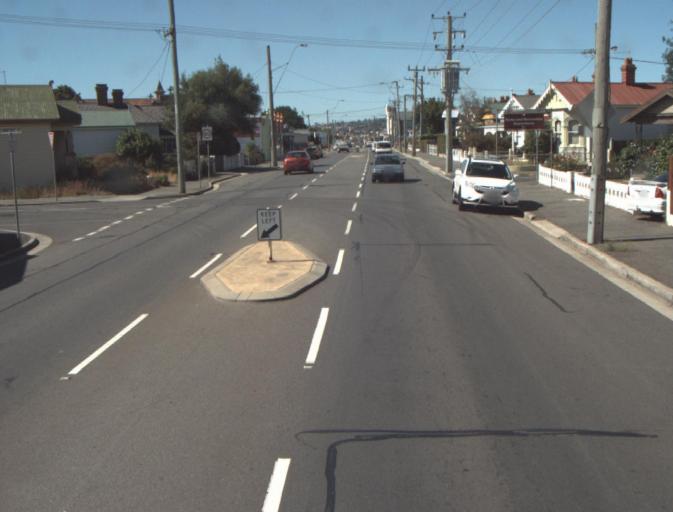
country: AU
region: Tasmania
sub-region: Launceston
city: Newnham
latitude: -41.4155
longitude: 147.1337
